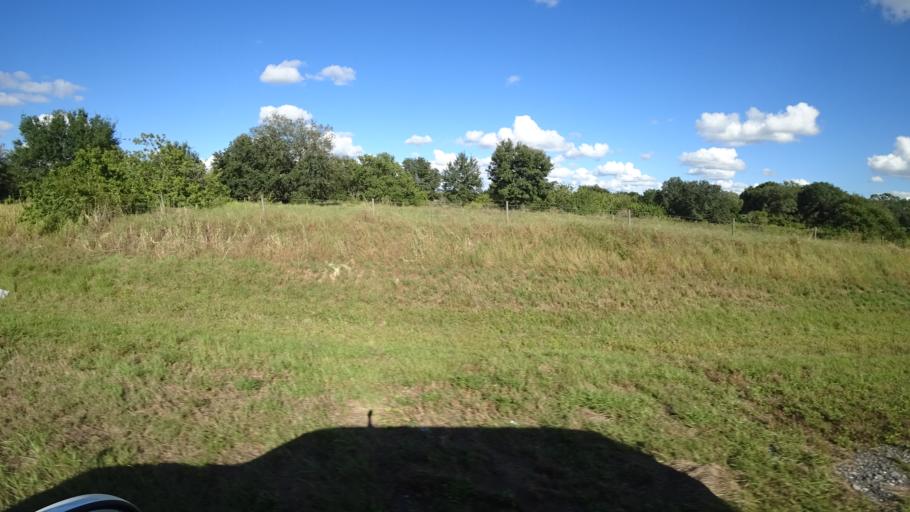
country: US
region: Florida
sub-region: Sarasota County
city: The Meadows
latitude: 27.4710
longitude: -82.3052
